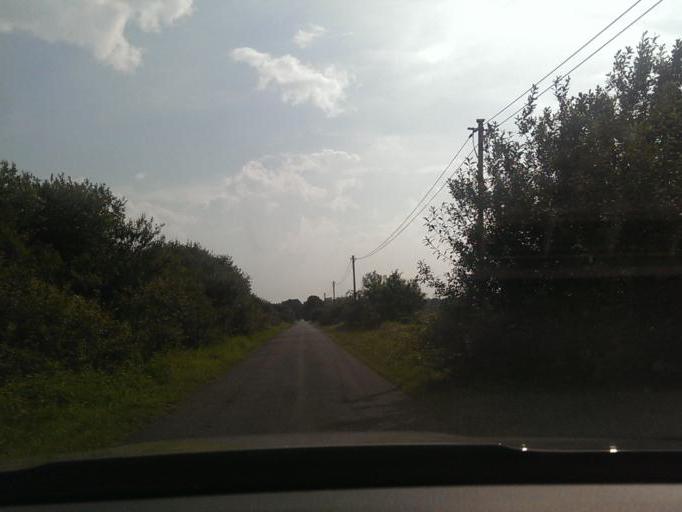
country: DE
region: Lower Saxony
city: Osterholz-Scharmbeck
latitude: 53.1683
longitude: 8.8026
